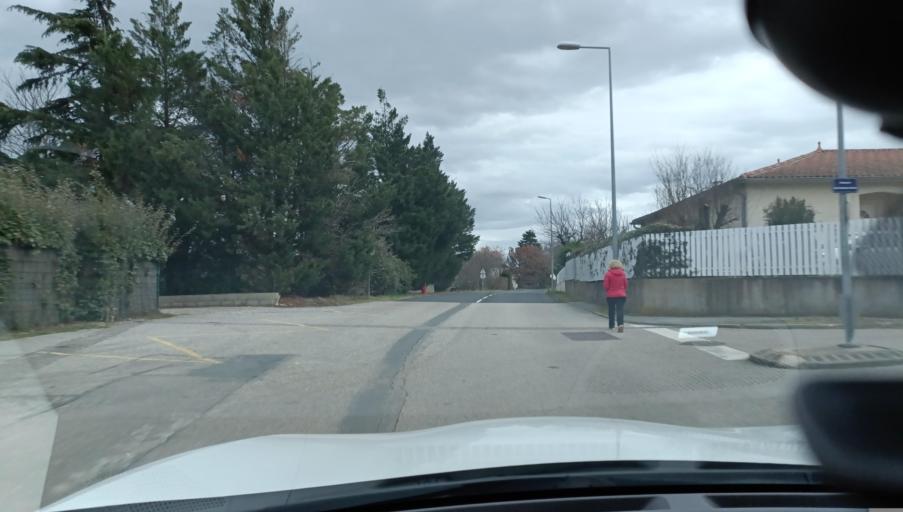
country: FR
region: Rhone-Alpes
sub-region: Departement de l'Isere
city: Chasse-sur-Rhone
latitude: 45.5831
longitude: 4.8195
